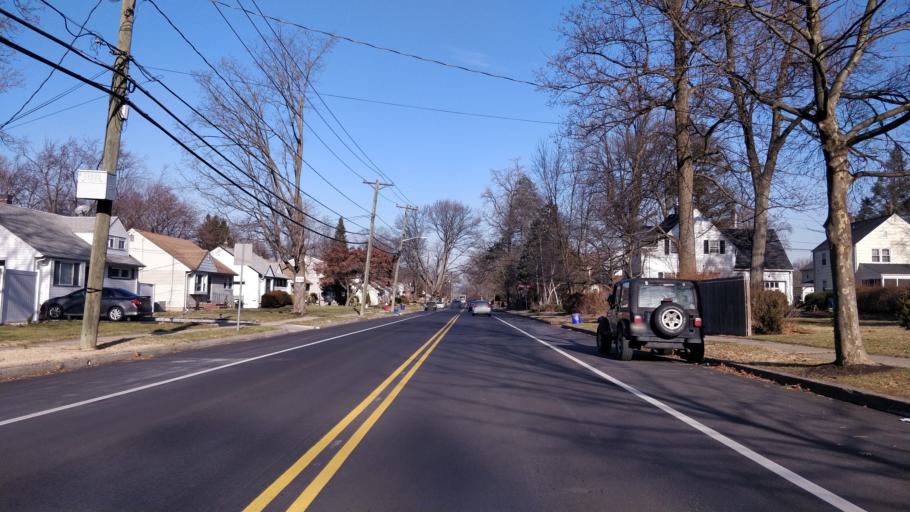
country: US
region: New Jersey
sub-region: Somerset County
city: North Plainfield
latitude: 40.6360
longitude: -74.4210
